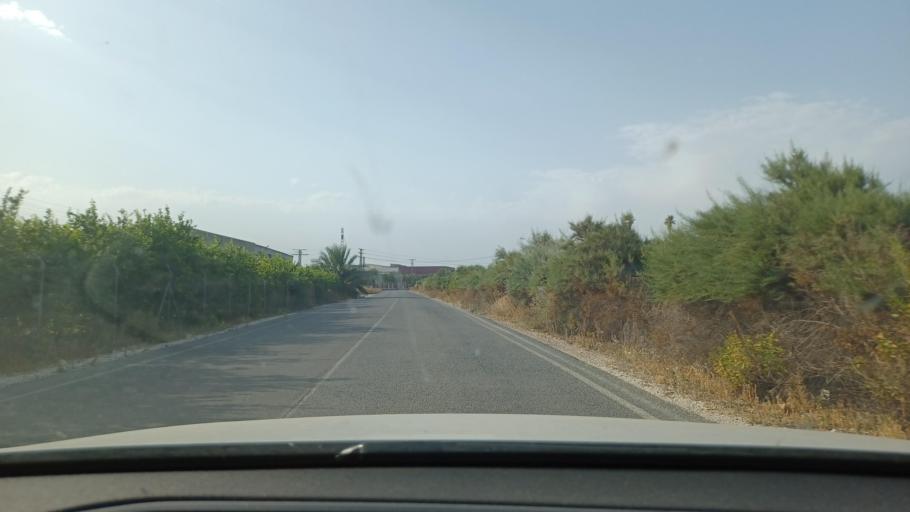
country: ES
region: Valencia
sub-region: Provincia de Alicante
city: Elche
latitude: 38.2472
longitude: -0.6909
